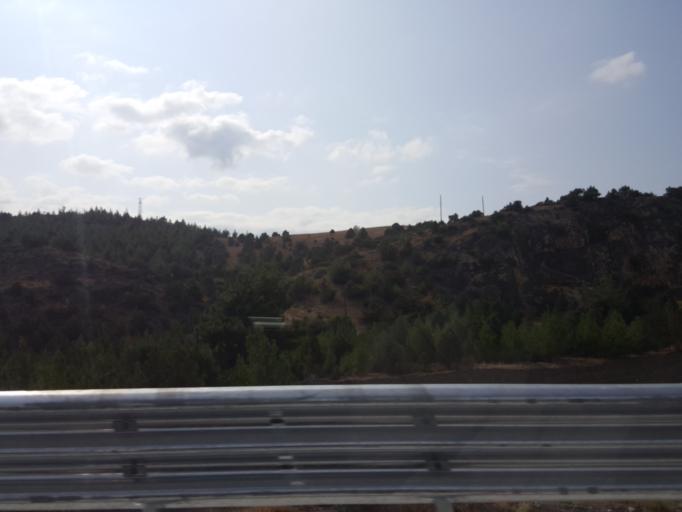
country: TR
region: Corum
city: Hacihamza
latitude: 41.0978
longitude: 34.3587
